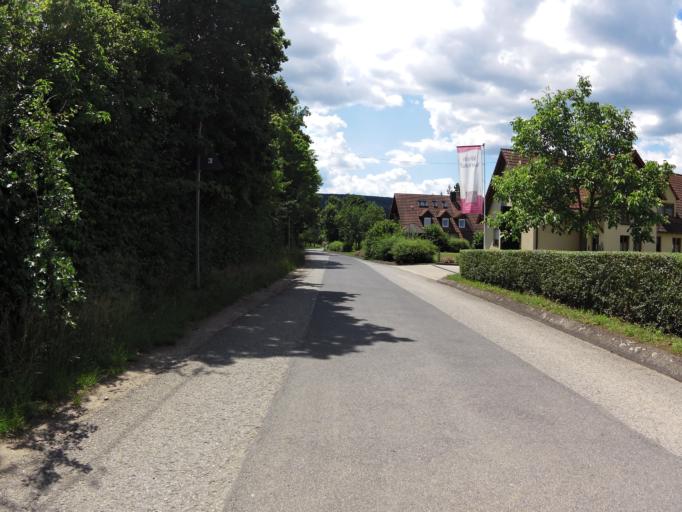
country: DE
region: Bavaria
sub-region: Regierungsbezirk Unterfranken
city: Thungersheim
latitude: 49.8843
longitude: 9.8481
